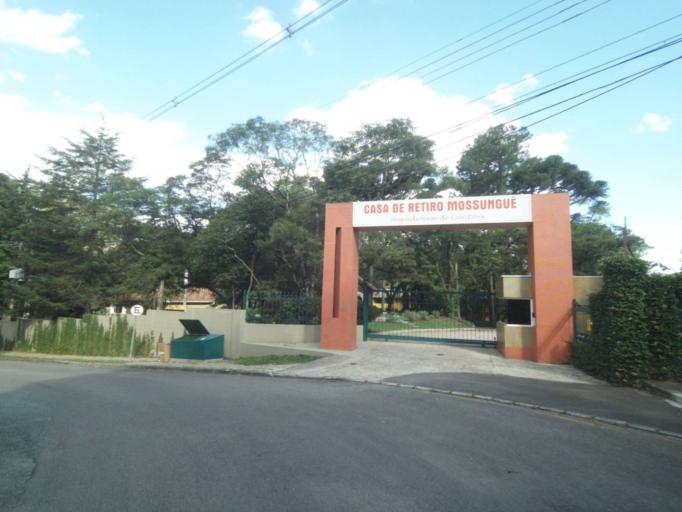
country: BR
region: Parana
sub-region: Curitiba
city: Curitiba
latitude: -25.4387
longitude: -49.3299
